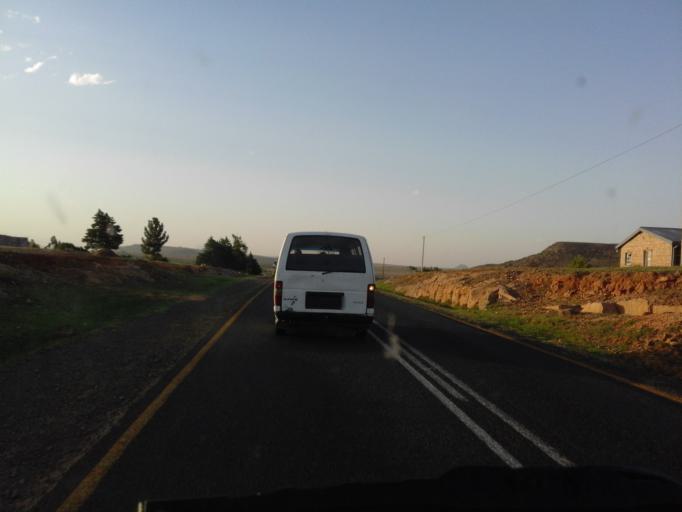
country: LS
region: Mafeteng
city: Mafeteng
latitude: -29.8831
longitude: 27.2460
